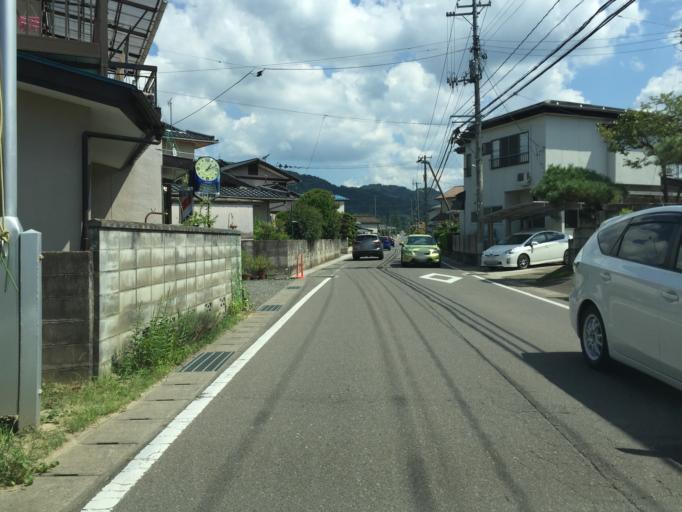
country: JP
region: Fukushima
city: Fukushima-shi
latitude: 37.7712
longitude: 140.5074
